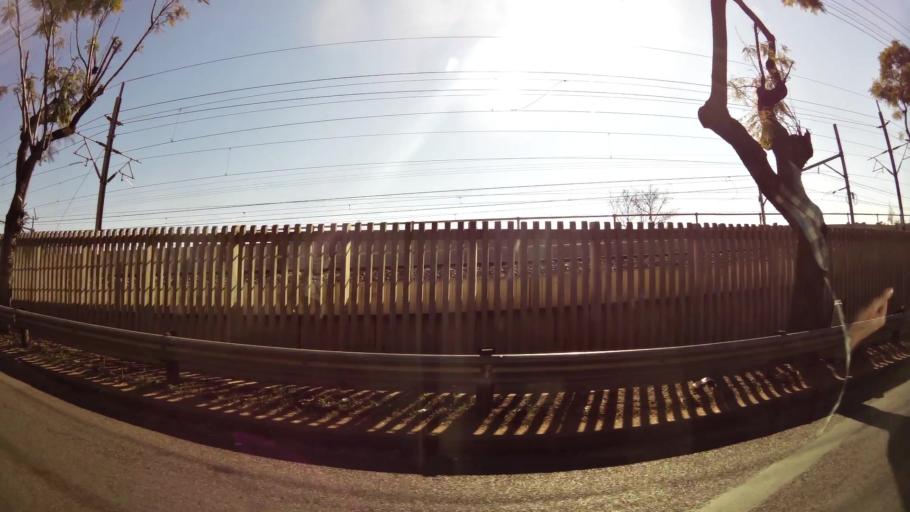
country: ZA
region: Gauteng
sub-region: City of Tshwane Metropolitan Municipality
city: Pretoria
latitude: -25.7603
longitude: 28.2181
